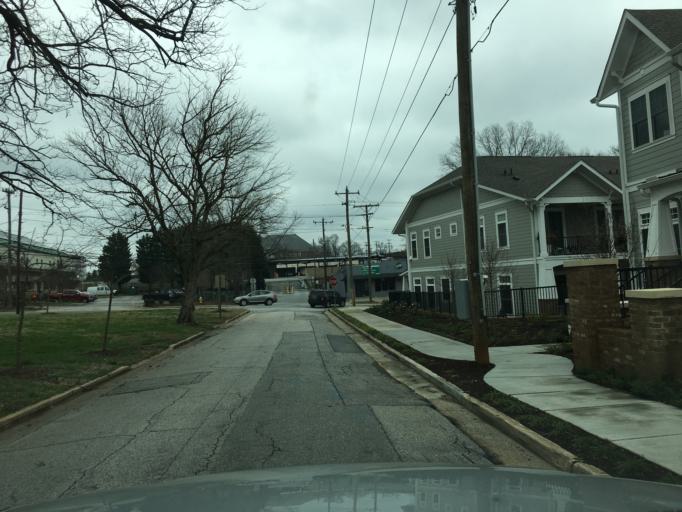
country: US
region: South Carolina
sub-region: Greenville County
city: Greenville
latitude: 34.8532
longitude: -82.4090
